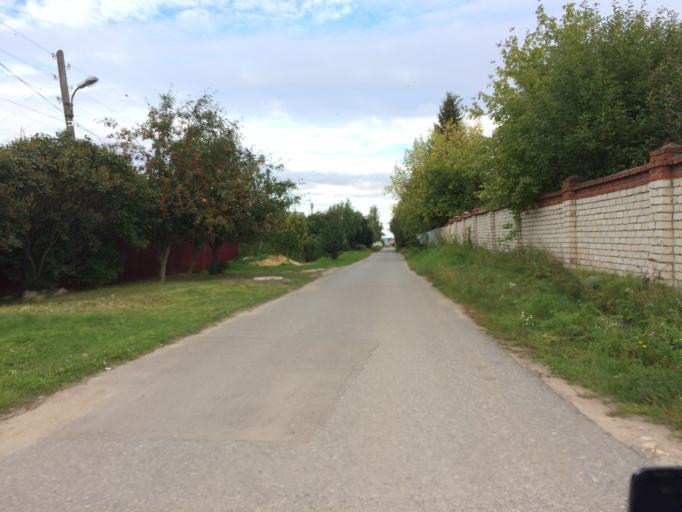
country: RU
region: Mariy-El
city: Yoshkar-Ola
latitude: 56.6642
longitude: 47.9957
